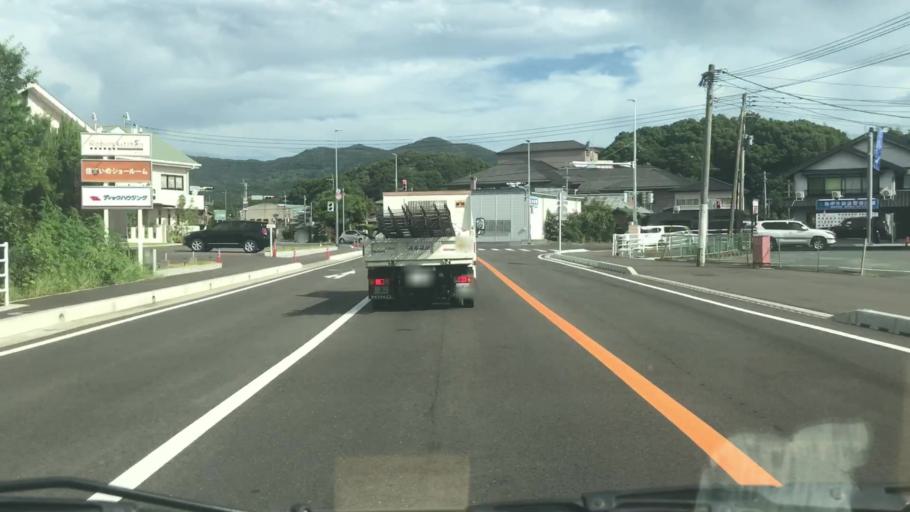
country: JP
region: Saga Prefecture
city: Takeocho-takeo
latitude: 33.2195
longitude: 130.0609
